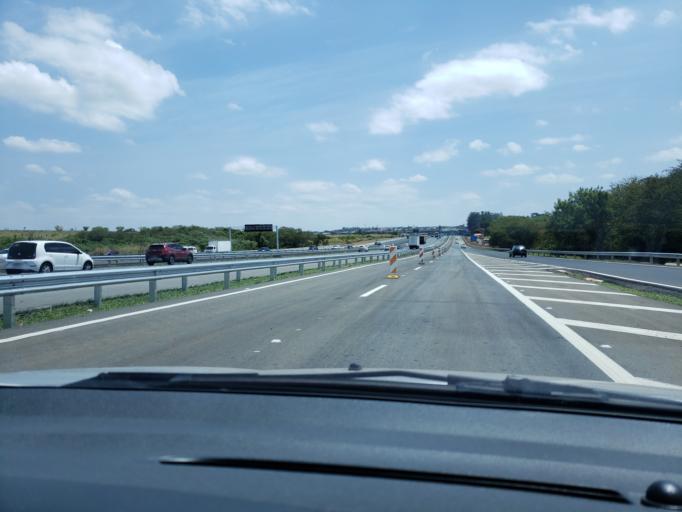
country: BR
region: Sao Paulo
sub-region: Campinas
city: Campinas
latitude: -22.8526
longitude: -47.1196
